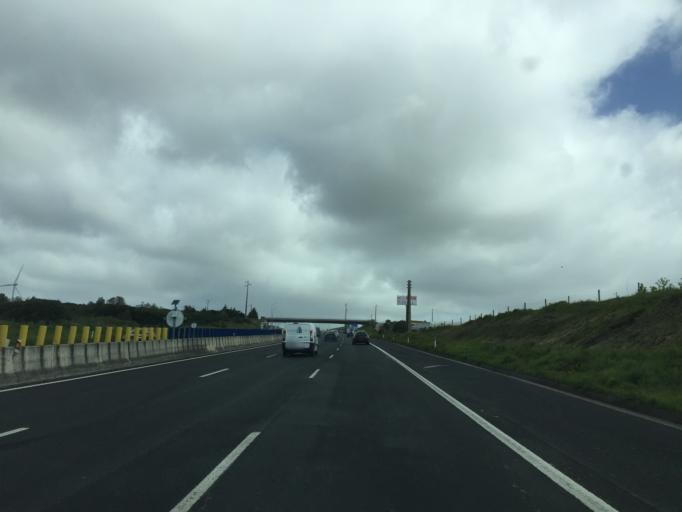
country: PT
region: Lisbon
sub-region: Loures
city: Loures
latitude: 38.8774
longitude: -9.1991
